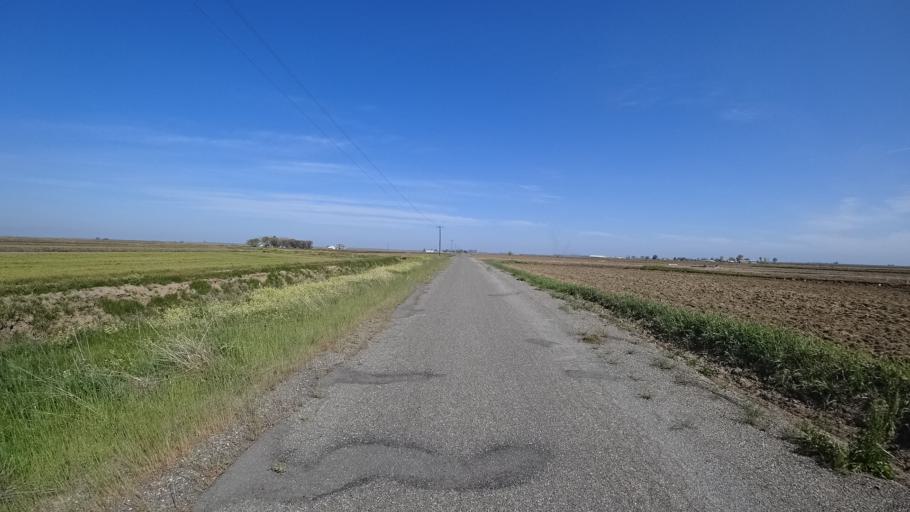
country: US
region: California
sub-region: Glenn County
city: Willows
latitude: 39.6046
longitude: -122.0743
